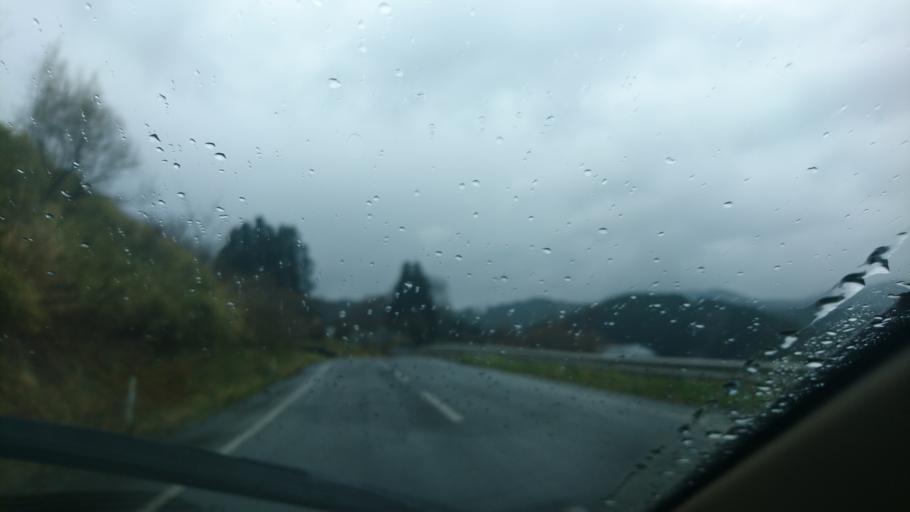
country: JP
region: Iwate
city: Ofunato
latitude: 38.9416
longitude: 141.4613
